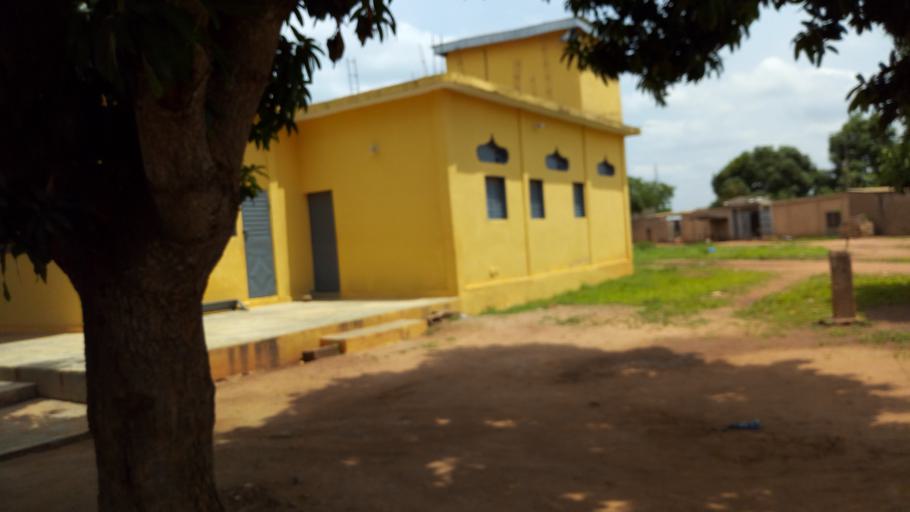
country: CI
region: Vallee du Bandama
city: Bouake
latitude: 7.7261
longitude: -4.9964
